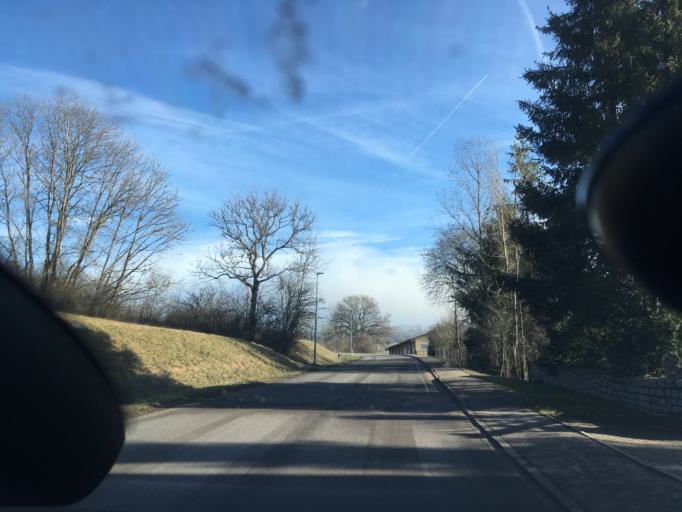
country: DE
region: Baden-Wuerttemberg
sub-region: Freiburg Region
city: Dogern
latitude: 47.6578
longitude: 8.1528
